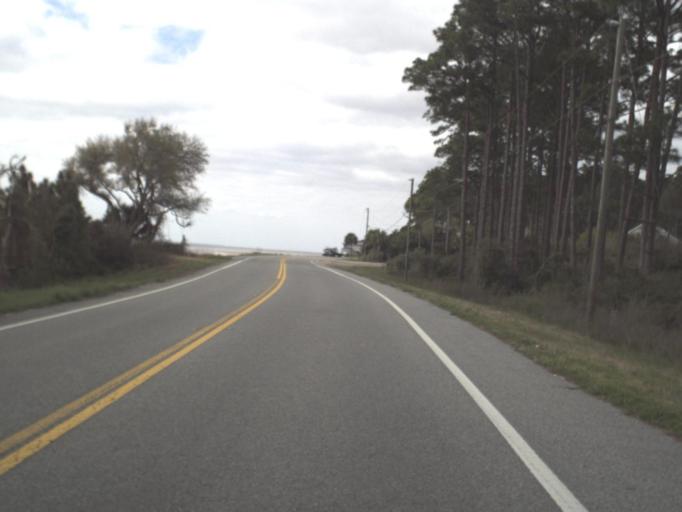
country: US
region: Florida
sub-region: Franklin County
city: Carrabelle
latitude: 29.8142
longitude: -84.7175
